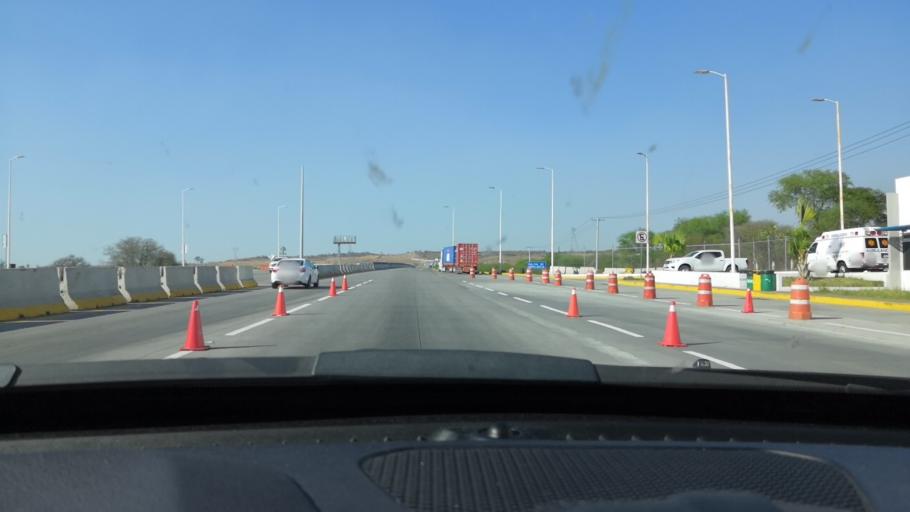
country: MX
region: Jalisco
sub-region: Zapotlanejo
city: La Mezquitera
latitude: 20.5730
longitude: -103.1012
